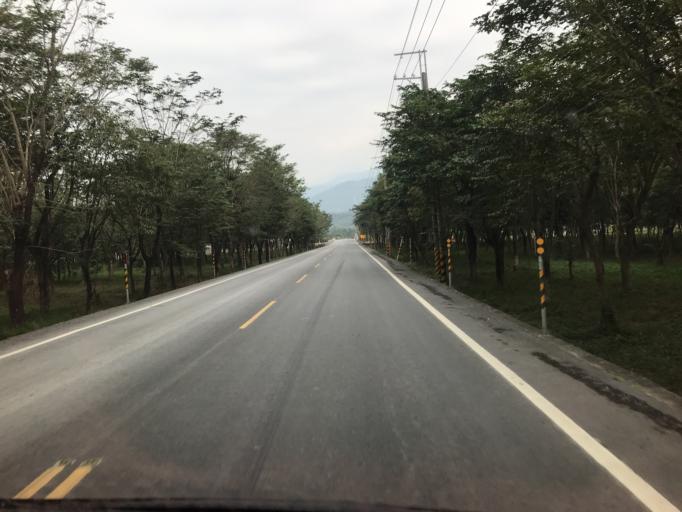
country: TW
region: Taiwan
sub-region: Pingtung
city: Pingtung
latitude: 22.4530
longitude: 120.6107
